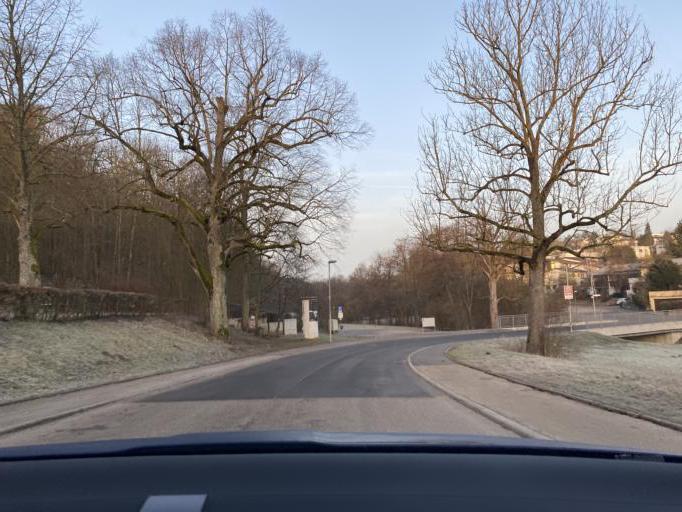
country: DE
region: Baden-Wuerttemberg
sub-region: Regierungsbezirk Stuttgart
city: Vaihingen an der Enz
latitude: 48.9137
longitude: 8.9410
